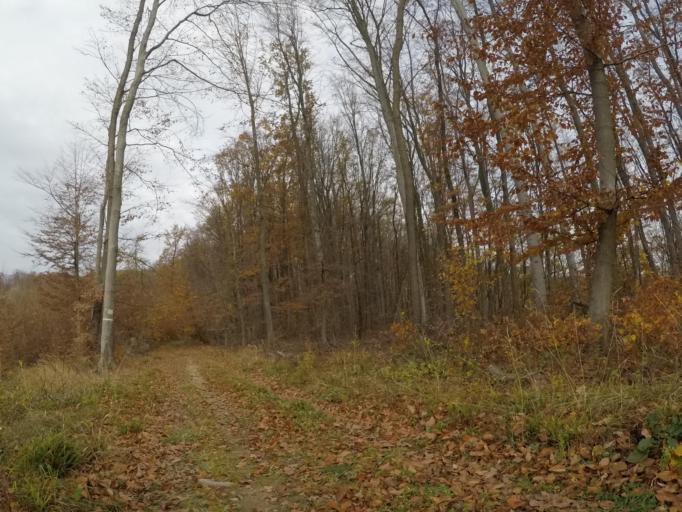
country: SK
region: Presovsky
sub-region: Okres Presov
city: Presov
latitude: 48.9594
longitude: 21.2116
